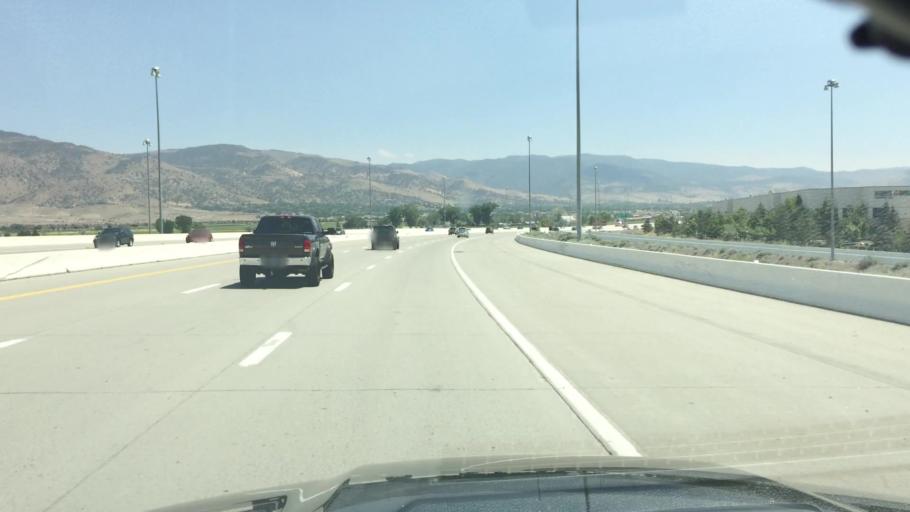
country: US
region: Nevada
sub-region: Washoe County
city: Sparks
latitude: 39.4222
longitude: -119.7504
